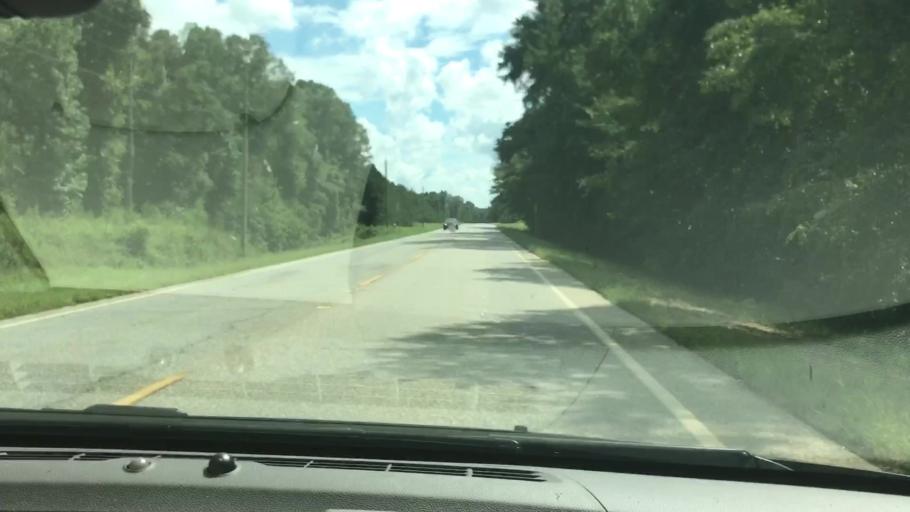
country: US
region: Georgia
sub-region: Clay County
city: Fort Gaines
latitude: 31.7097
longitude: -85.0415
